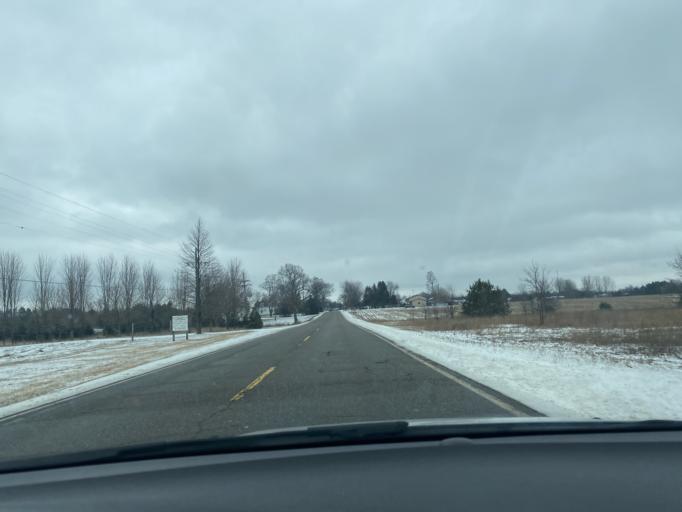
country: US
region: Michigan
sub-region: Lapeer County
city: Barnes Lake-Millers Lake
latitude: 43.2063
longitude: -83.2603
